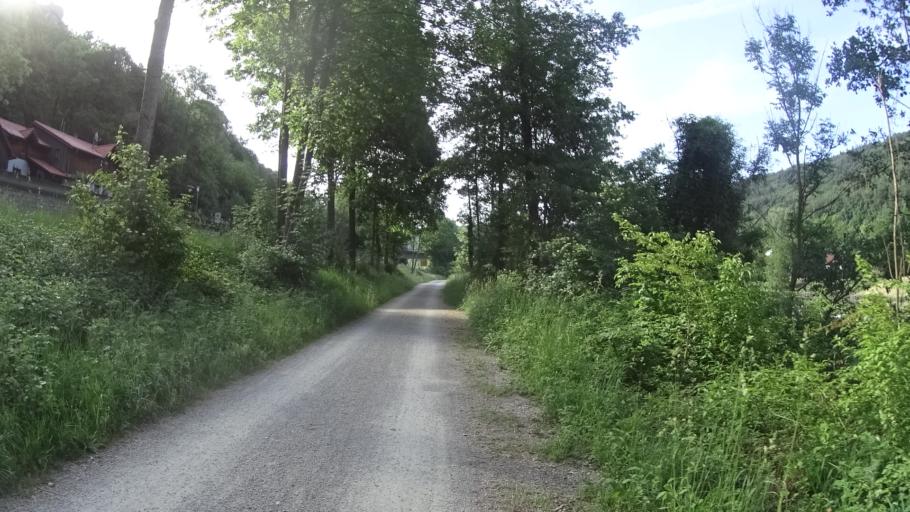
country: DE
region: Bavaria
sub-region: Lower Bavaria
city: Essing
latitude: 48.9477
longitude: 11.7406
